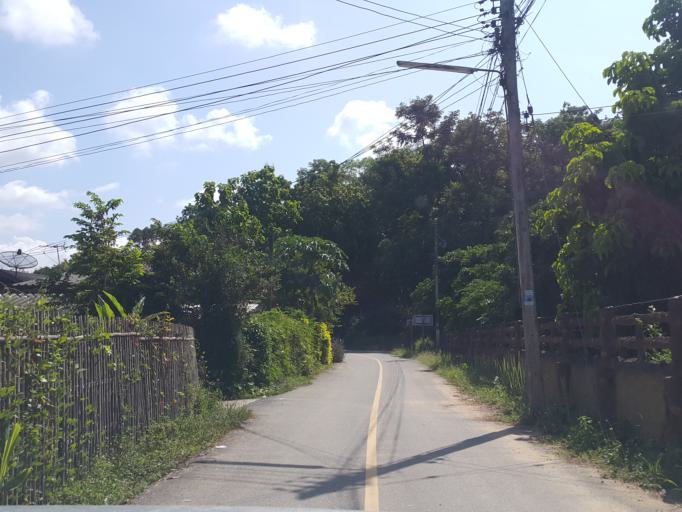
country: TH
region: Chiang Mai
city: San Kamphaeng
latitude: 18.7515
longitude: 99.1712
